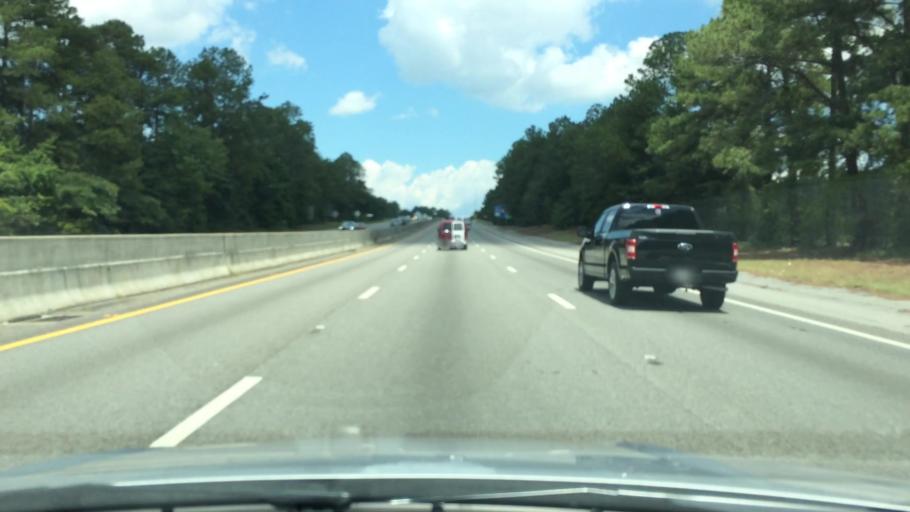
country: US
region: South Carolina
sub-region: Lexington County
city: Springdale
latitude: 33.9732
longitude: -81.1031
